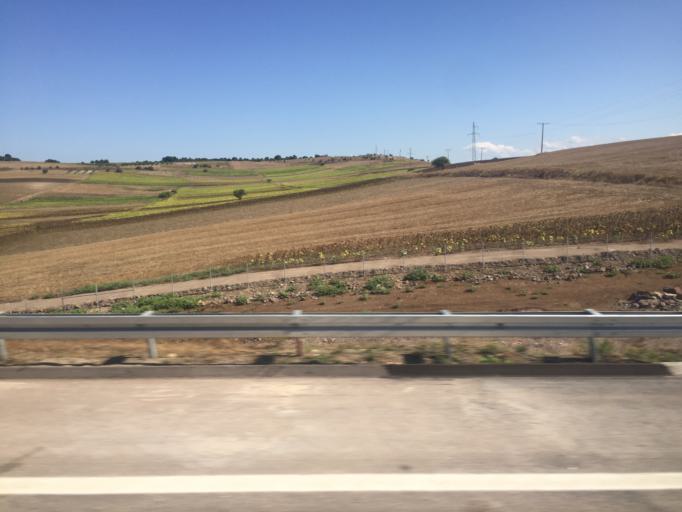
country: TR
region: Bursa
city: Mahmudiye
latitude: 40.2682
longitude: 28.6359
